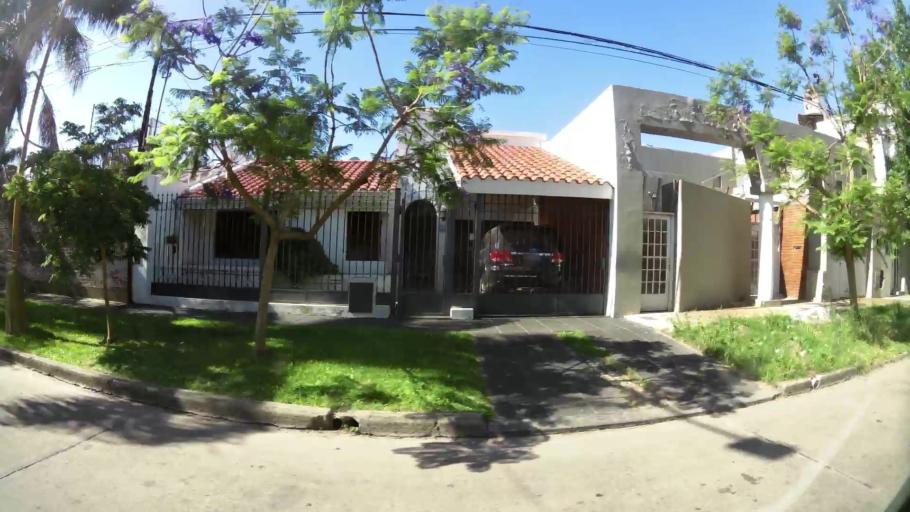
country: AR
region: Santa Fe
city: Santa Fe de la Vera Cruz
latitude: -31.6093
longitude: -60.6719
